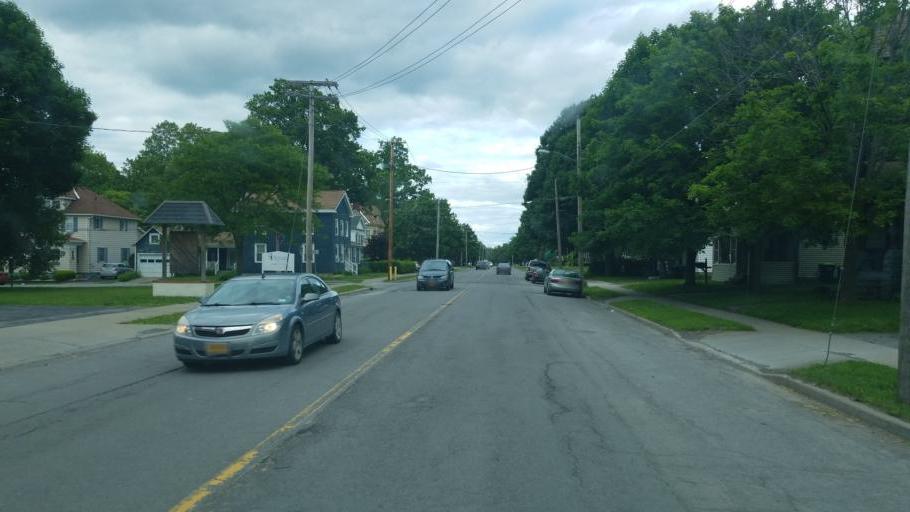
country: US
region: New York
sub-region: Herkimer County
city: Mohawk
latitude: 43.0119
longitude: -75.0025
